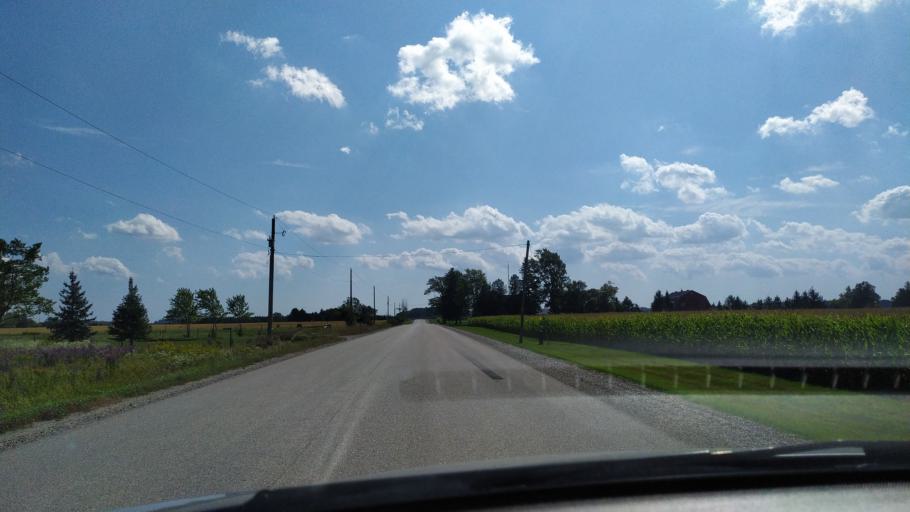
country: CA
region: Ontario
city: Stratford
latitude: 43.3006
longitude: -80.9429
